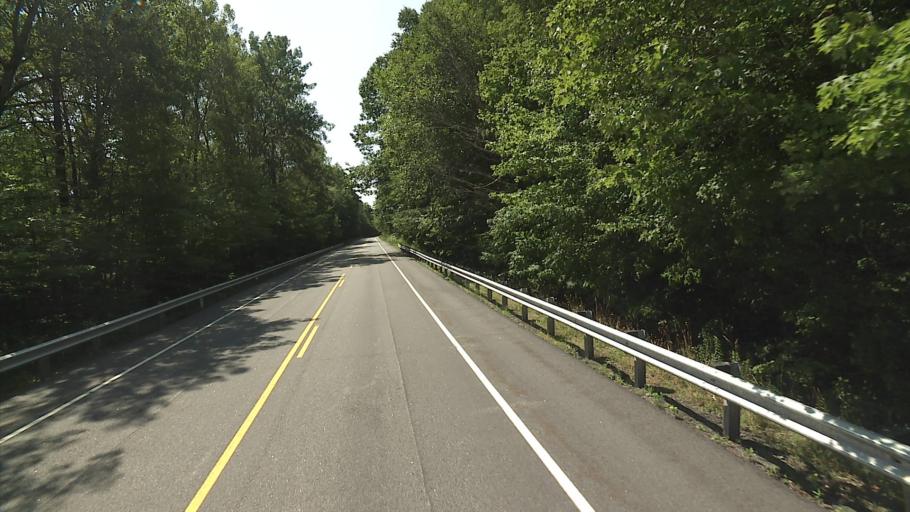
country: US
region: Connecticut
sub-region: Litchfield County
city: Winchester Center
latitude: 41.8806
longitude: -73.1700
